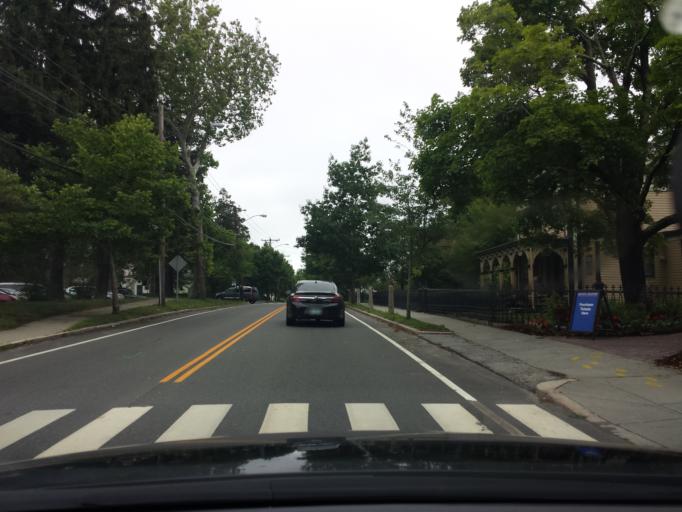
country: US
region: Connecticut
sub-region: New London County
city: Mystic
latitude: 41.3623
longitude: -71.9634
